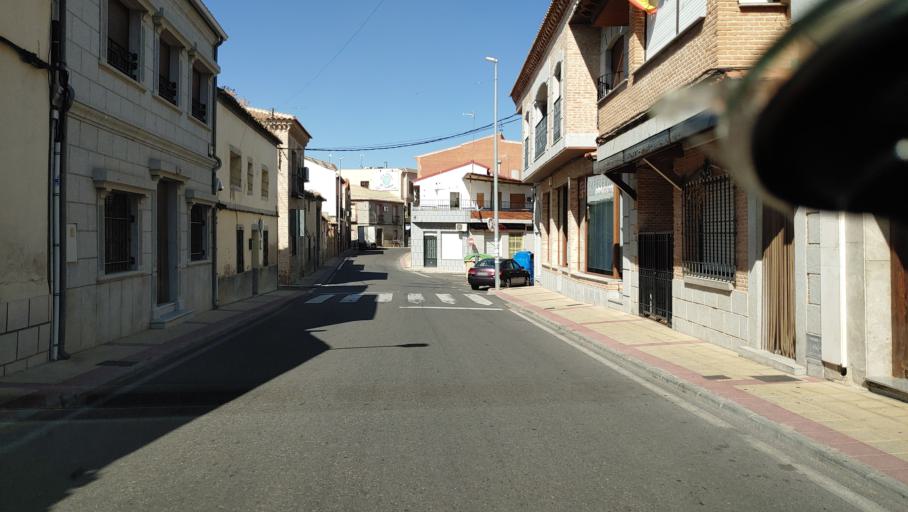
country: ES
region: Castille-La Mancha
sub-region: Province of Toledo
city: Pulgar
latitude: 39.6936
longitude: -4.1540
